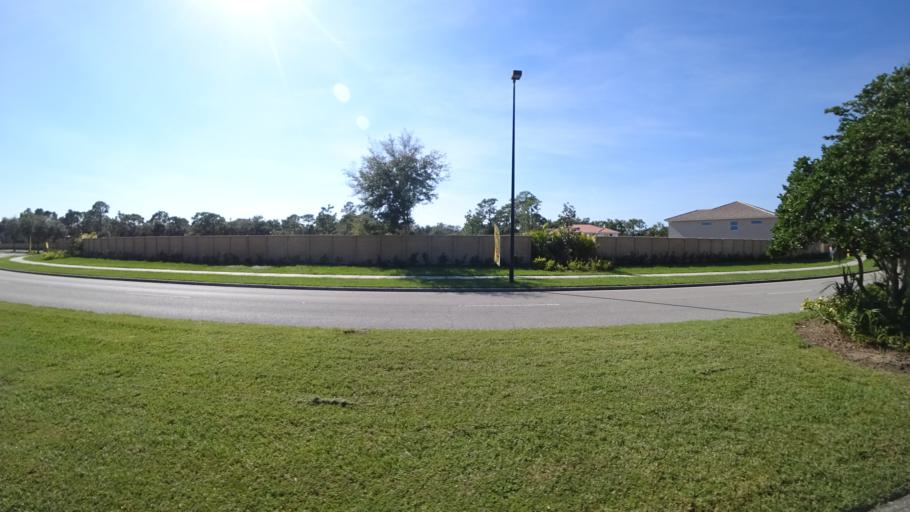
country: US
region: Florida
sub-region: Sarasota County
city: The Meadows
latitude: 27.4002
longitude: -82.4473
